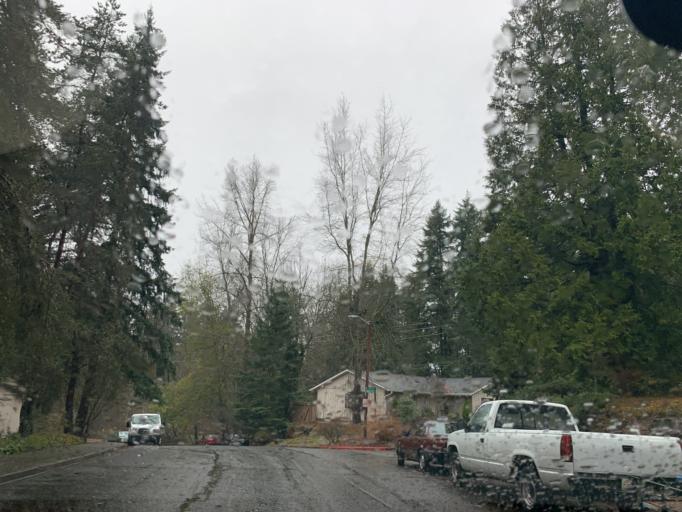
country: US
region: Washington
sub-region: King County
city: Kingsgate
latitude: 47.7368
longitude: -122.1767
